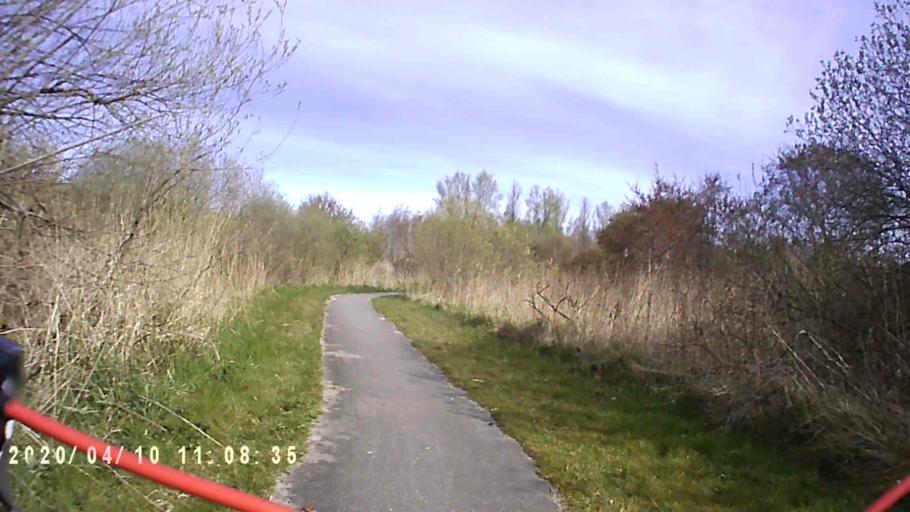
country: NL
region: Groningen
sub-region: Gemeente De Marne
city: Ulrum
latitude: 53.3914
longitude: 6.2419
